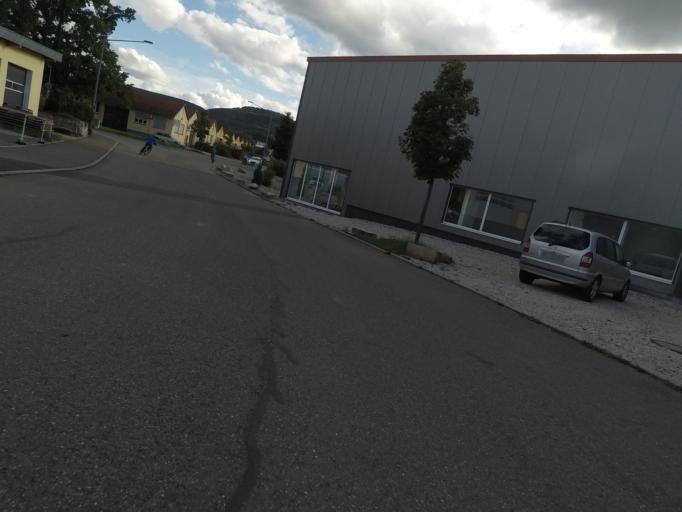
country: DE
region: Baden-Wuerttemberg
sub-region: Tuebingen Region
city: Pfullingen
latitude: 48.4725
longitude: 9.2230
